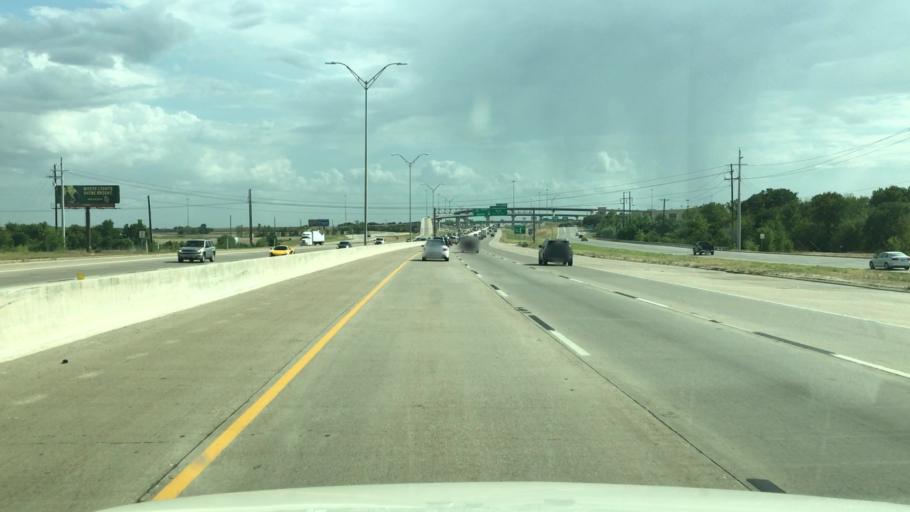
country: US
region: Texas
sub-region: McLennan County
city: Beverly Hills
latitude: 31.5034
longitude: -97.1453
